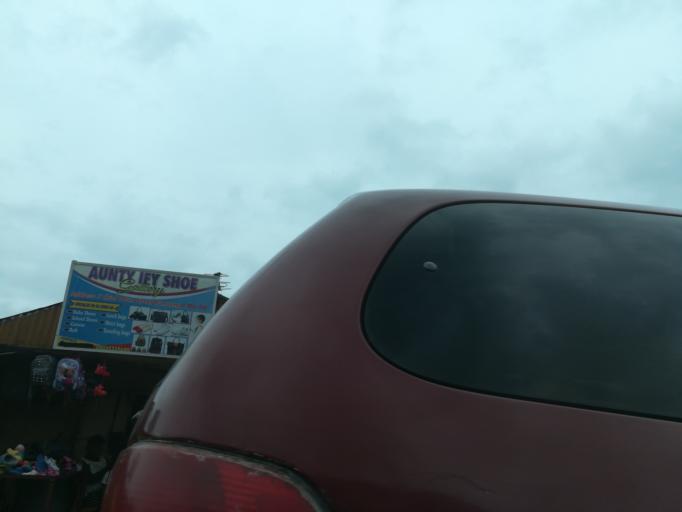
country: NG
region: Rivers
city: Port Harcourt
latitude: 4.8264
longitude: 7.0270
